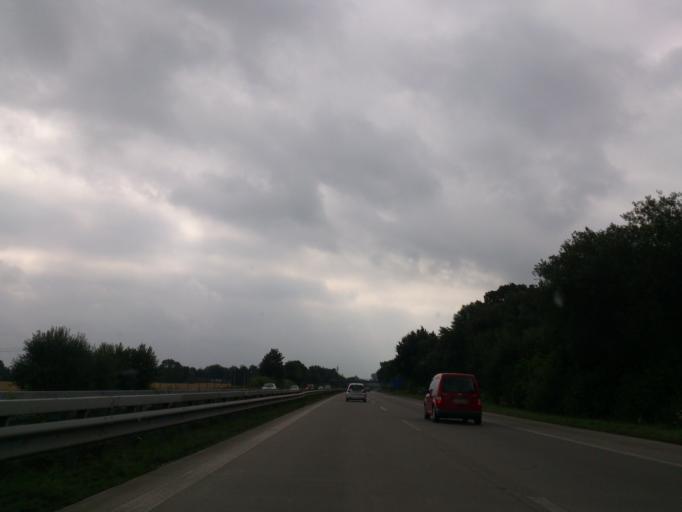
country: DE
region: Schleswig-Holstein
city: Klein Offenseth-Sparrieshoop
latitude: 53.8043
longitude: 9.6804
